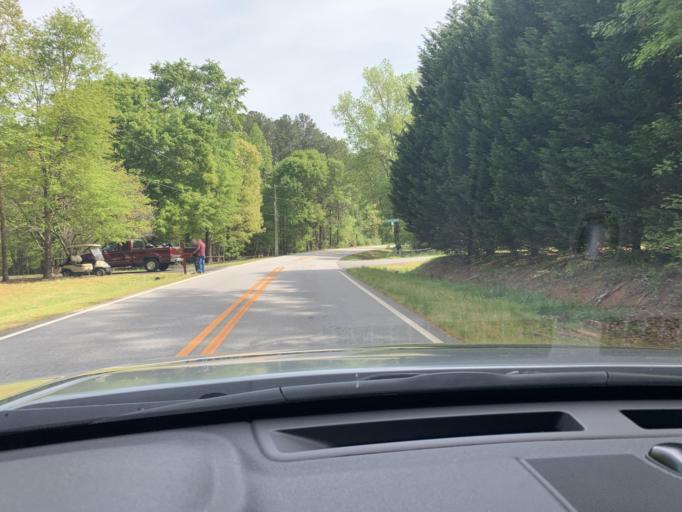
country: US
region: Georgia
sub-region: Oconee County
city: Watkinsville
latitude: 33.8512
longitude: -83.4649
